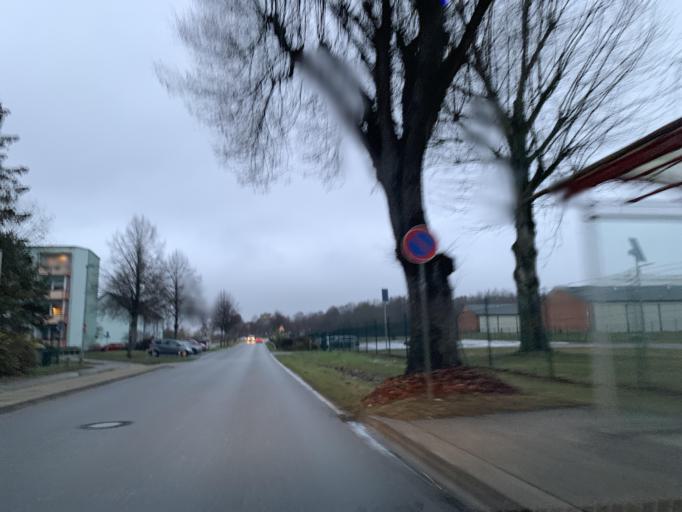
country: DE
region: Mecklenburg-Vorpommern
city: Neubrandenburg
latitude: 53.5260
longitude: 13.2839
